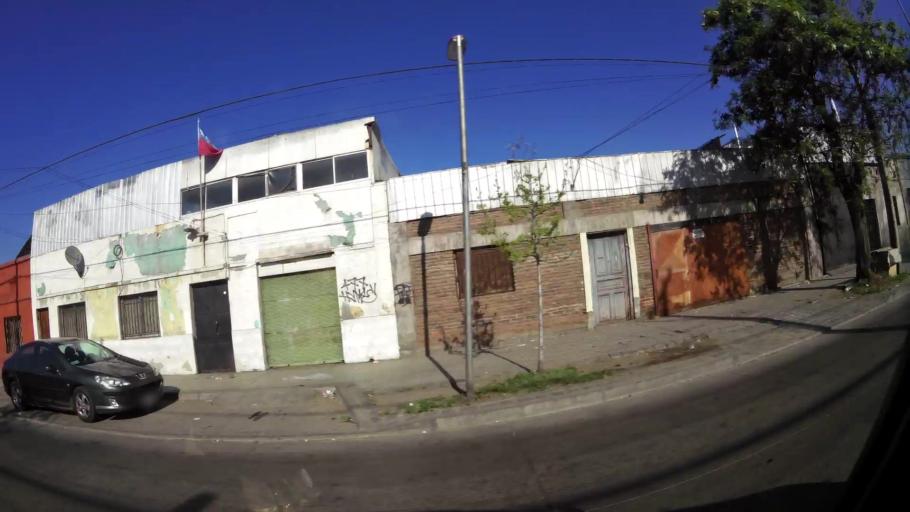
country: CL
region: Santiago Metropolitan
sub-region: Provincia de Santiago
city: Santiago
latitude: -33.4767
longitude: -70.6318
